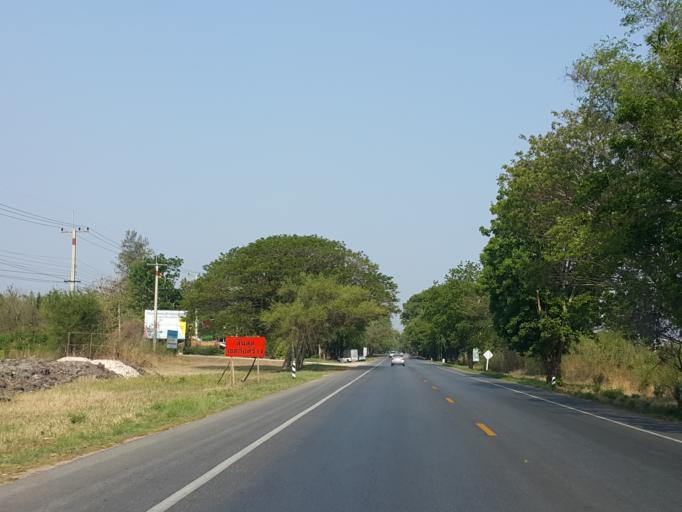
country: TH
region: Kanchanaburi
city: Sai Yok
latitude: 14.0900
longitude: 99.3101
